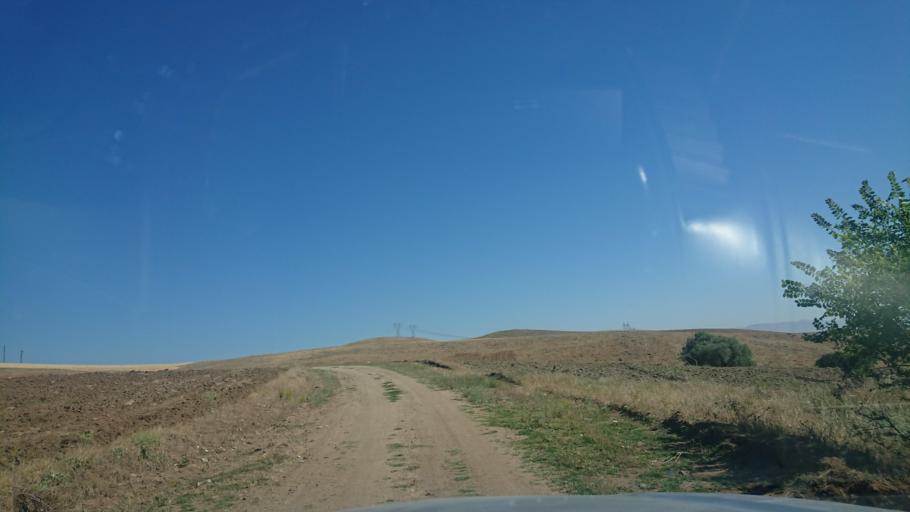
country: TR
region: Aksaray
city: Agacoren
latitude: 38.9092
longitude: 33.8988
